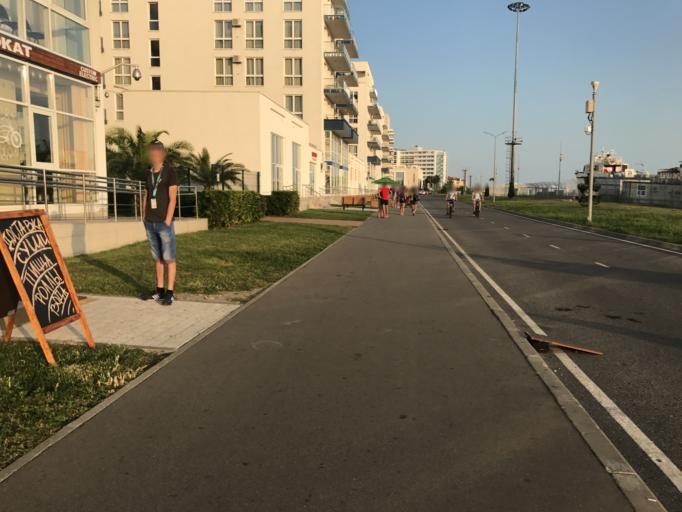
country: RU
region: Krasnodarskiy
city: Adler
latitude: 43.4125
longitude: 39.9332
